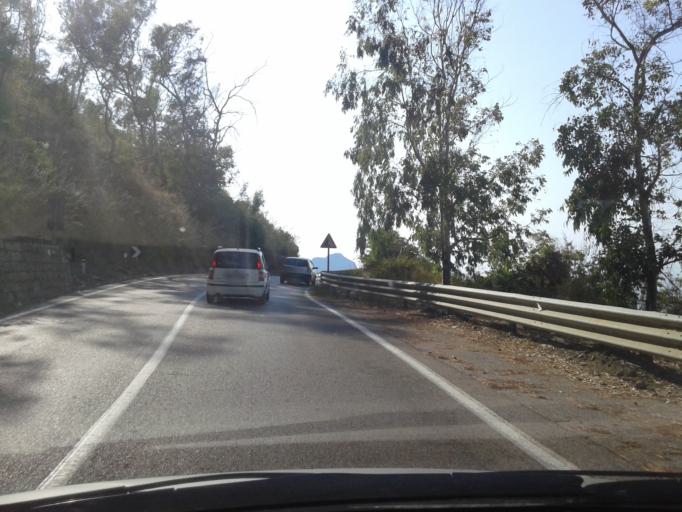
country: IT
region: Sicily
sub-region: Palermo
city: Pollina
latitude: 38.0160
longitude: 14.1186
